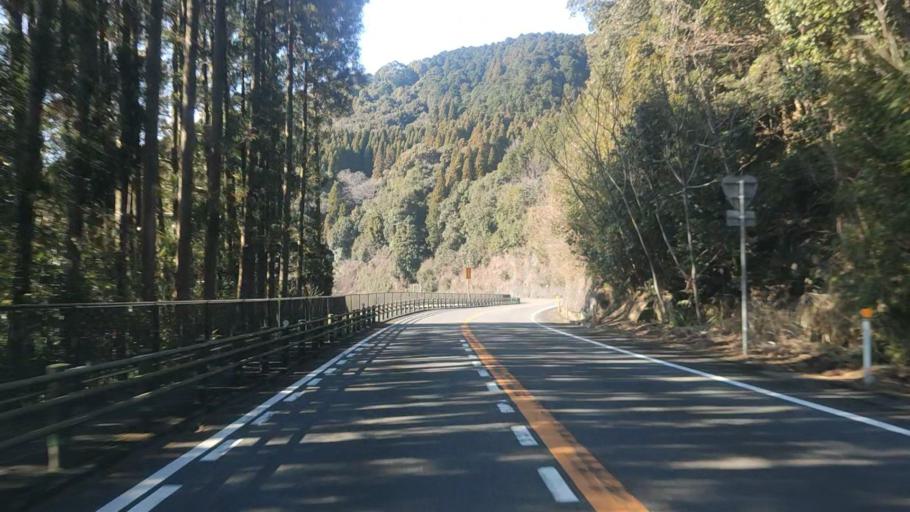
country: JP
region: Oita
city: Usuki
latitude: 33.0075
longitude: 131.7143
